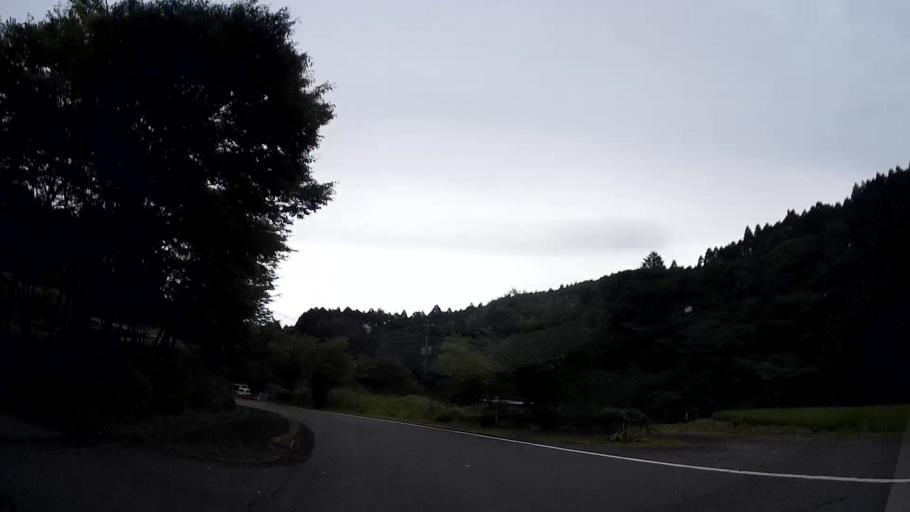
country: JP
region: Kumamoto
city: Kikuchi
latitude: 33.0708
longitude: 130.9105
